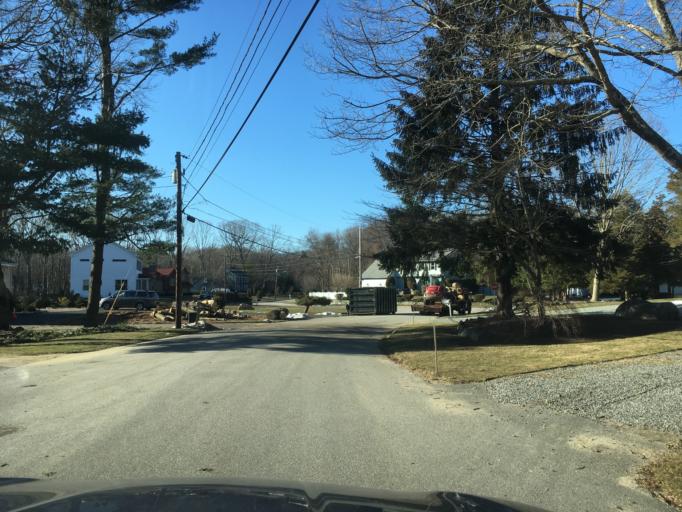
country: US
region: Rhode Island
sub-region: Kent County
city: East Greenwich
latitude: 41.6497
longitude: -71.4914
